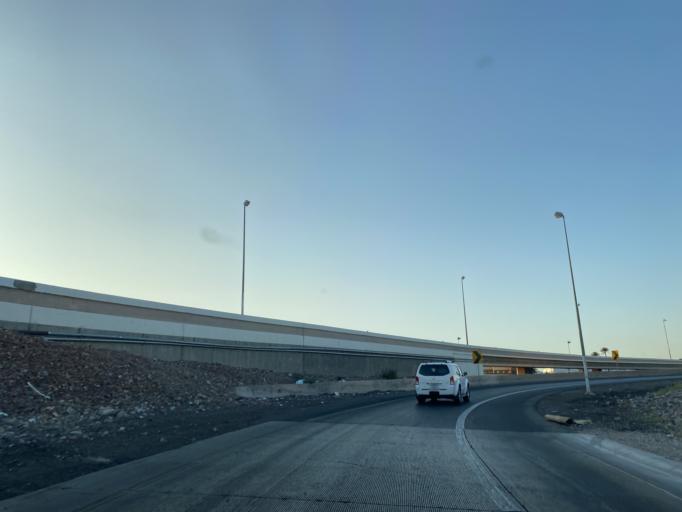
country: US
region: Nevada
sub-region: Clark County
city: Paradise
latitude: 36.0626
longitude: -115.1787
